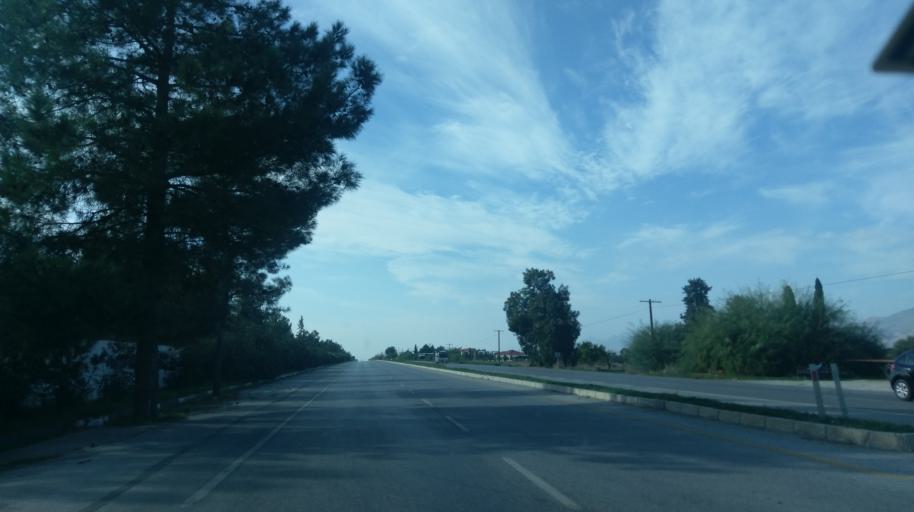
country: CY
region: Larnaka
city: Athienou
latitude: 35.2082
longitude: 33.5871
